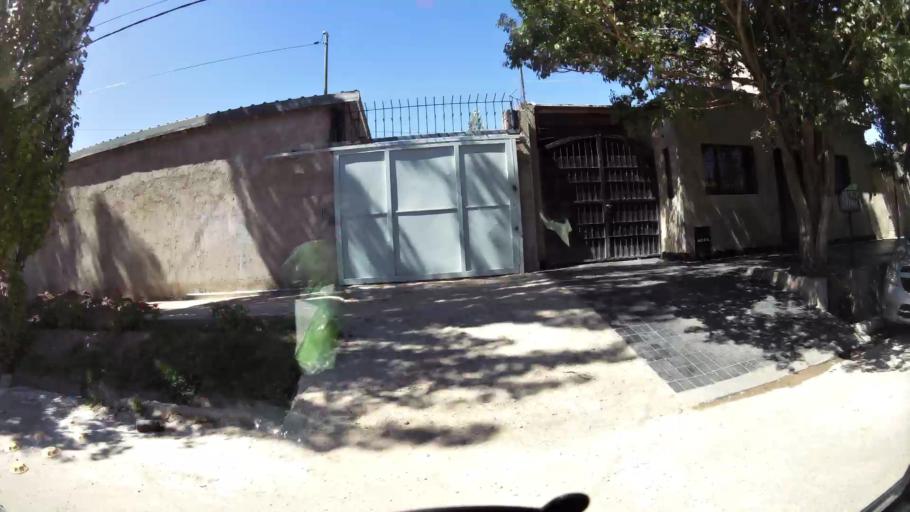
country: AR
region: Mendoza
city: Las Heras
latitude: -32.8546
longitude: -68.8479
